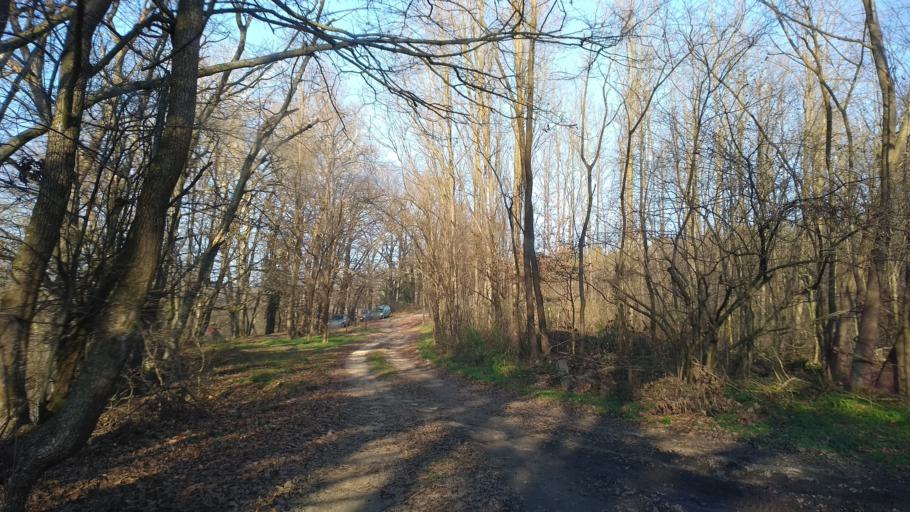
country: HU
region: Somogy
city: Barcs
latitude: 45.9474
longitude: 17.5221
